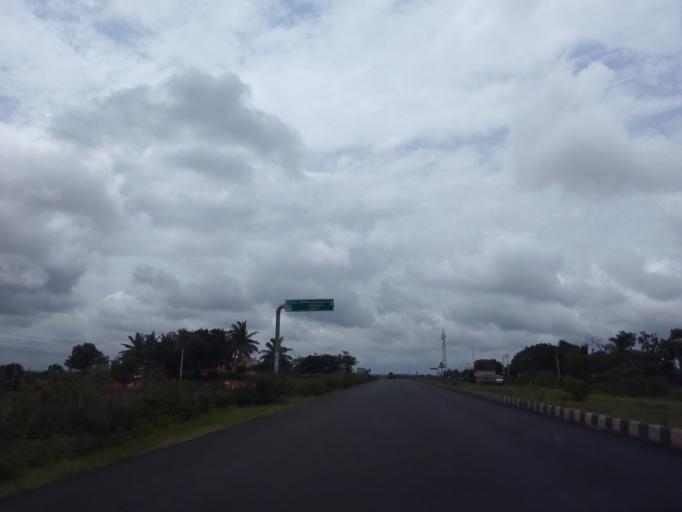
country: IN
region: Karnataka
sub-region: Haveri
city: Byadgi
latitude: 14.6965
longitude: 75.5272
